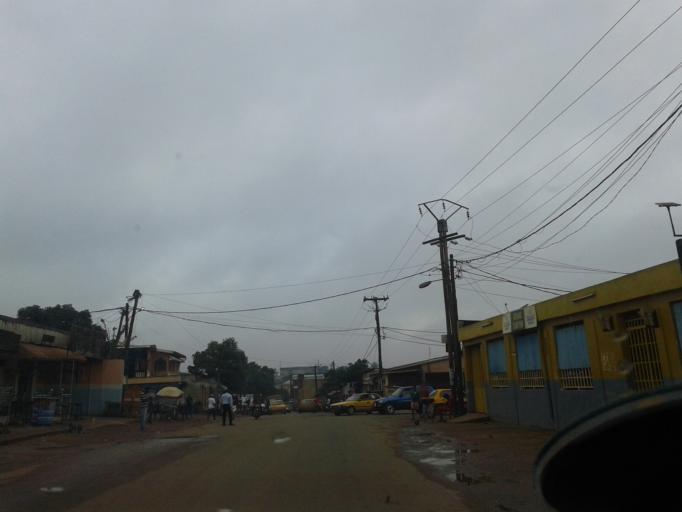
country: CM
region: Centre
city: Yaounde
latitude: 3.9068
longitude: 11.5302
